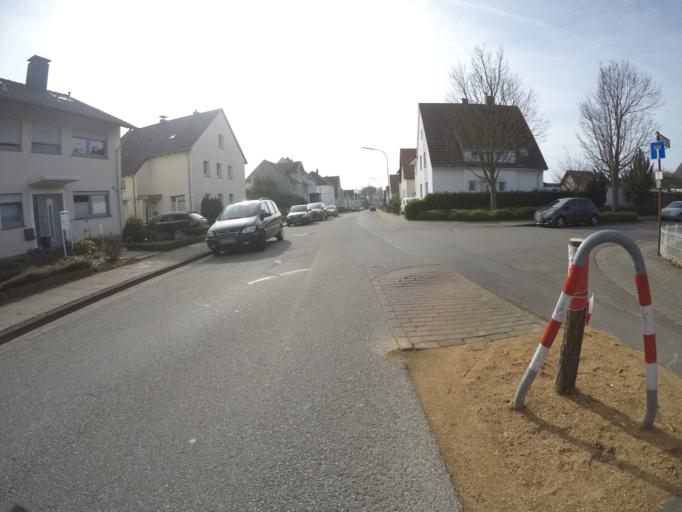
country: DE
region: North Rhine-Westphalia
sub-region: Regierungsbezirk Detmold
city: Herford
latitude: 52.1139
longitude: 8.6466
